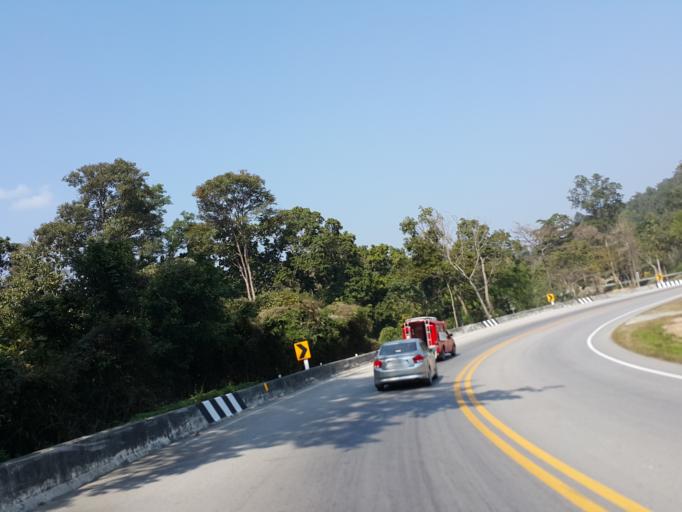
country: TH
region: Chiang Mai
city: Mae On
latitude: 18.9441
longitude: 99.2344
